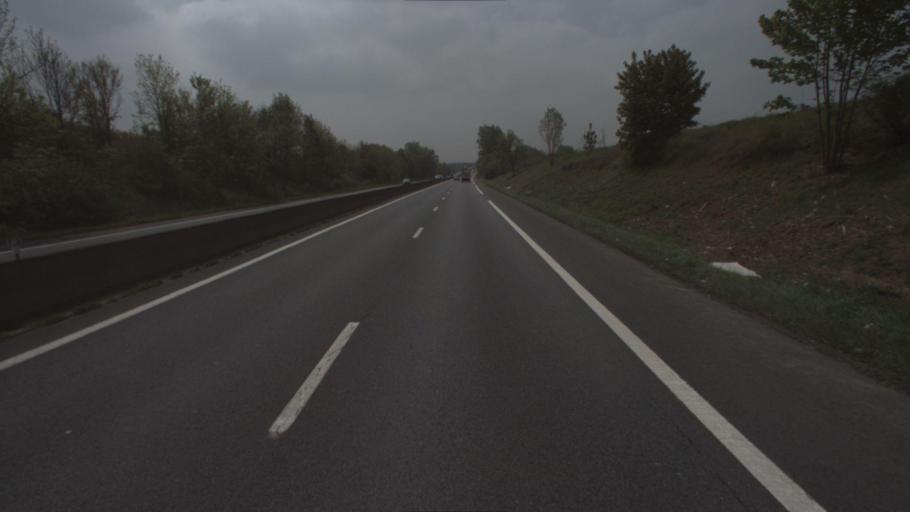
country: FR
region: Ile-de-France
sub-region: Departement de Seine-et-Marne
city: Longperrier
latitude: 49.0180
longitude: 2.6605
